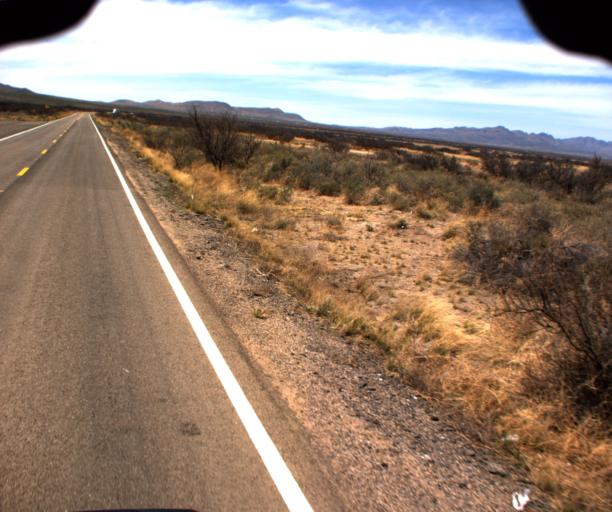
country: US
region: Arizona
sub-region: Cochise County
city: Willcox
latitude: 32.1396
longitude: -109.9216
